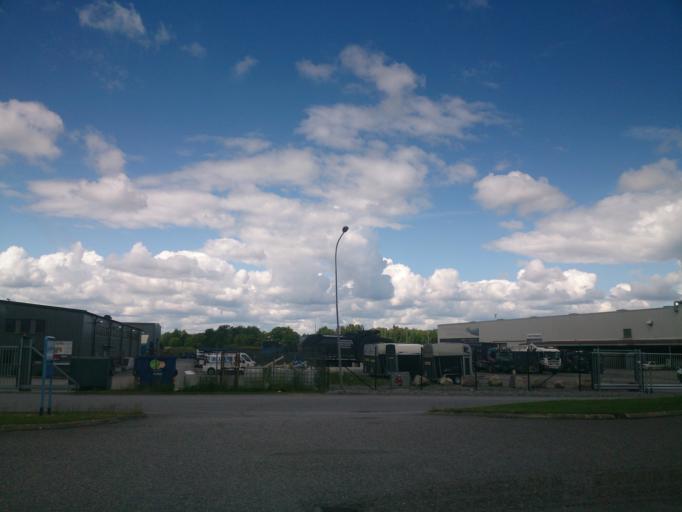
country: SE
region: OEstergoetland
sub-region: Norrkopings Kommun
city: Norrkoping
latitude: 58.6169
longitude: 16.1516
